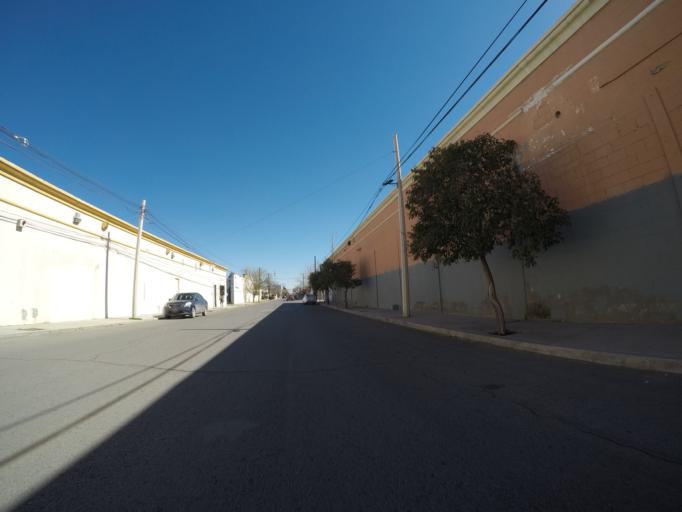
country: MX
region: Chihuahua
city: Ciudad Juarez
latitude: 31.7326
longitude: -106.4485
